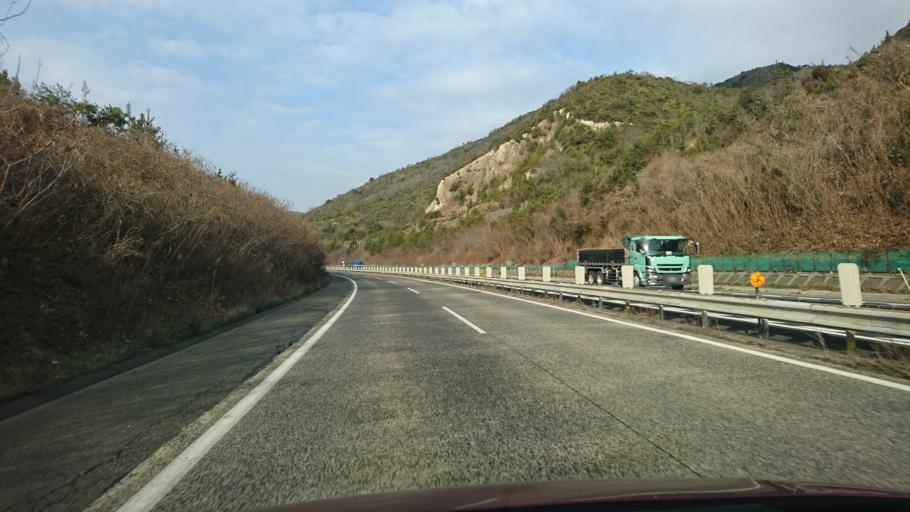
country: JP
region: Hyogo
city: Kariya
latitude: 34.7805
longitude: 134.3427
